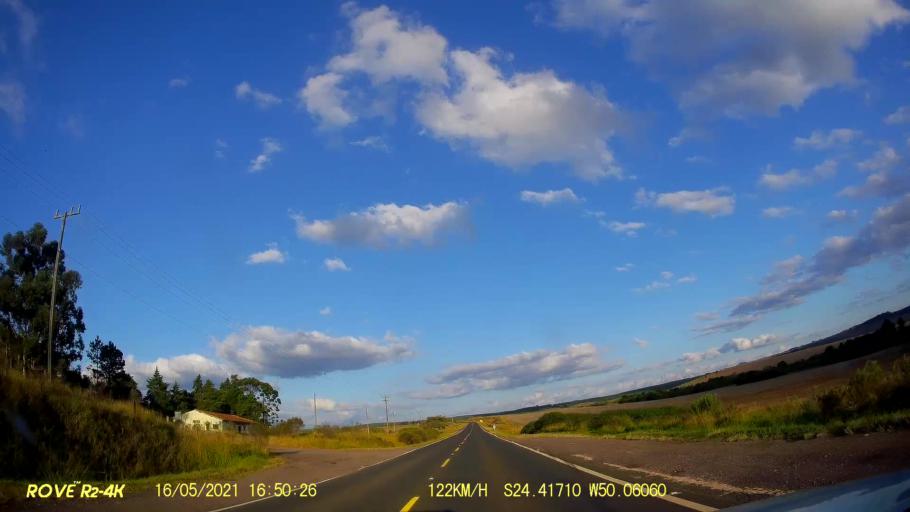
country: BR
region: Parana
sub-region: Pirai Do Sul
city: Pirai do Sul
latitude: -24.4173
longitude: -50.0606
